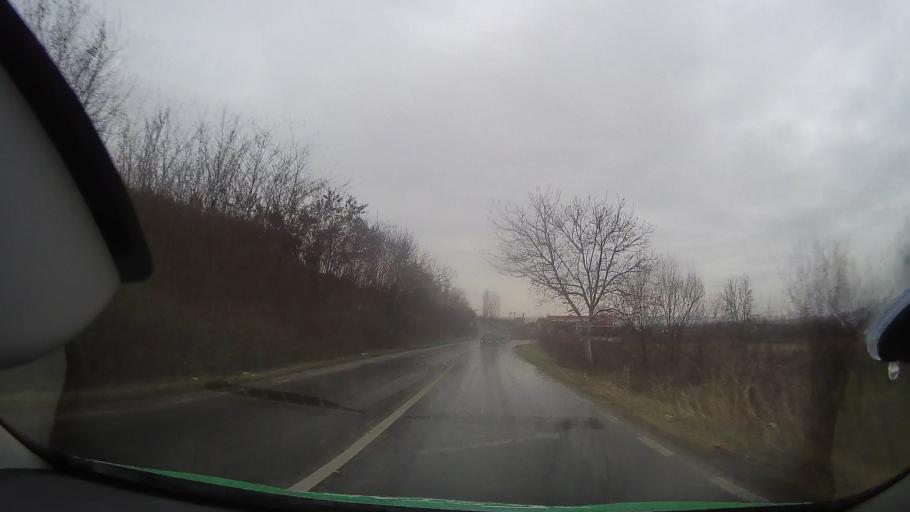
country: RO
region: Bihor
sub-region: Comuna Holod
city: Vintere
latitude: 46.7655
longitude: 22.1858
